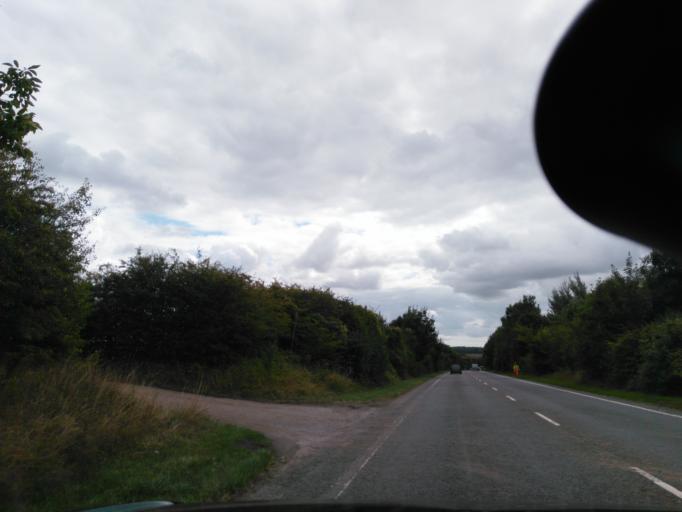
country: GB
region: England
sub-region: Dorset
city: Blandford Forum
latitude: 50.8723
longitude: -2.1550
